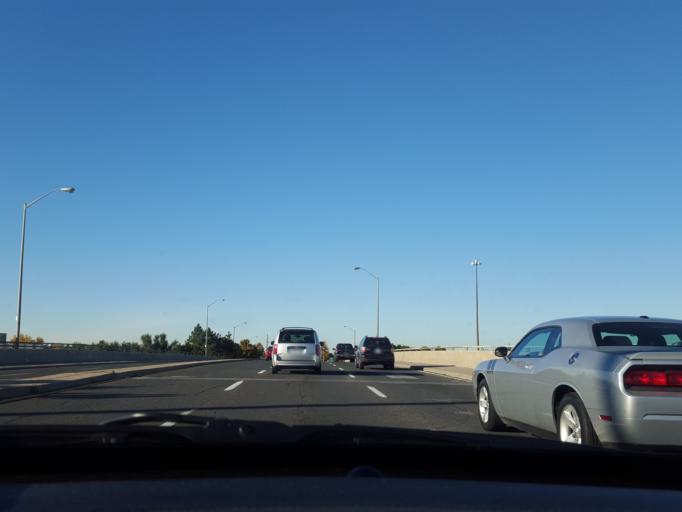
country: CA
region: Ontario
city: Scarborough
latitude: 43.7784
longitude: -79.2644
